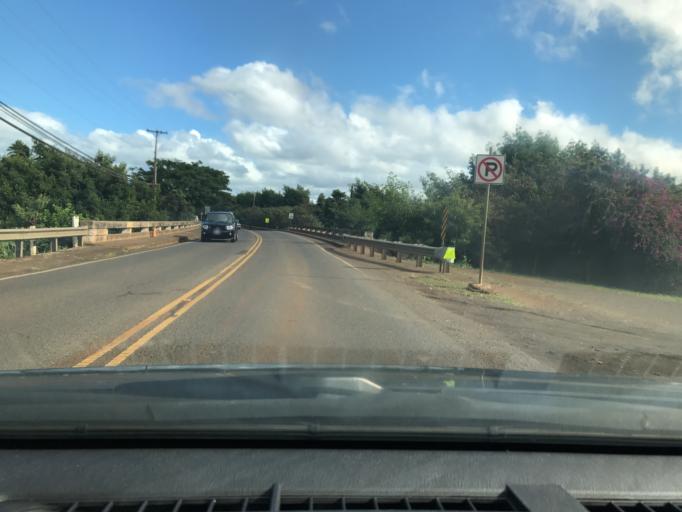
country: US
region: Hawaii
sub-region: Honolulu County
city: Waialua
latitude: 21.5758
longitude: -158.1205
